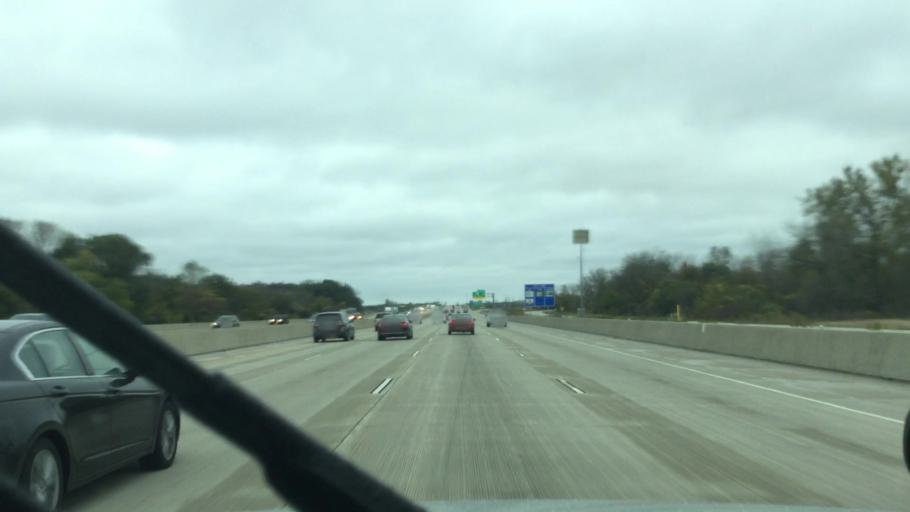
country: US
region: Wisconsin
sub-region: Kenosha County
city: Pleasant Prairie
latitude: 42.5529
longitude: -87.9527
